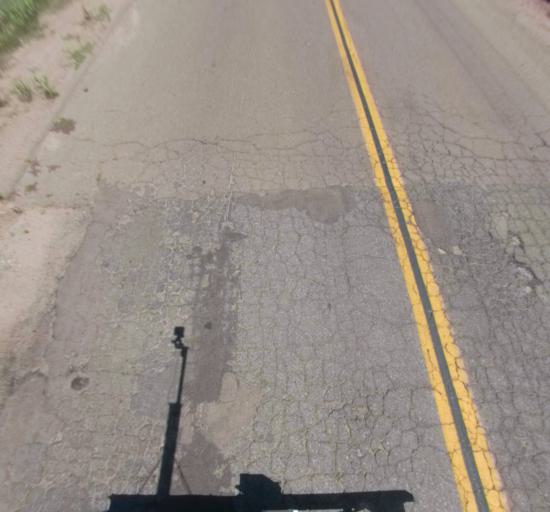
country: US
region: California
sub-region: Madera County
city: Chowchilla
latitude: 37.0242
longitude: -120.3106
